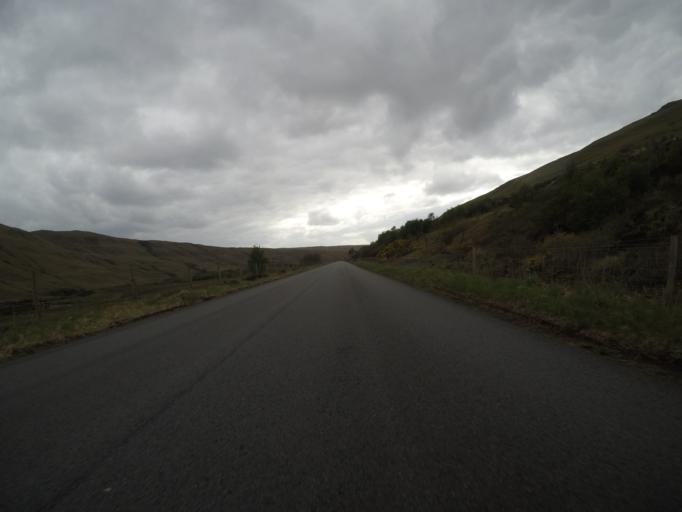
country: GB
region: Scotland
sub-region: Highland
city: Isle of Skye
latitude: 57.3002
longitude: -6.2552
